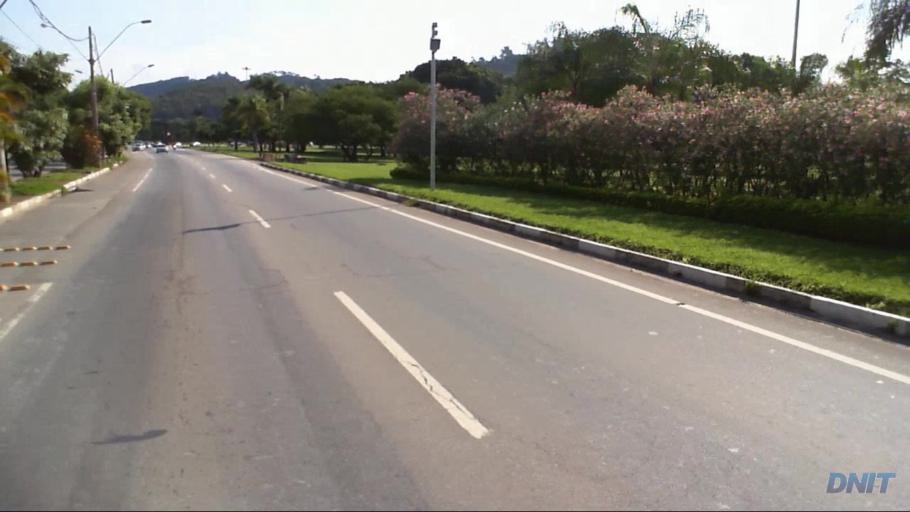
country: BR
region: Minas Gerais
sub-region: Ipatinga
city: Ipatinga
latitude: -19.4848
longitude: -42.5531
